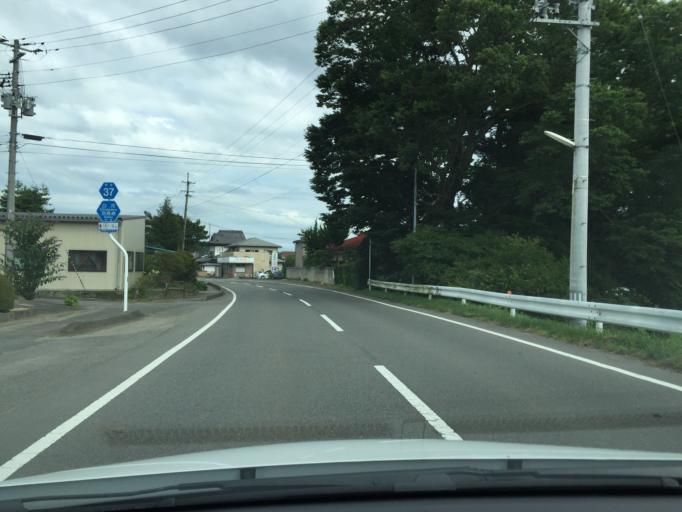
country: JP
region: Tochigi
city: Kuroiso
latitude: 37.1881
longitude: 140.1373
